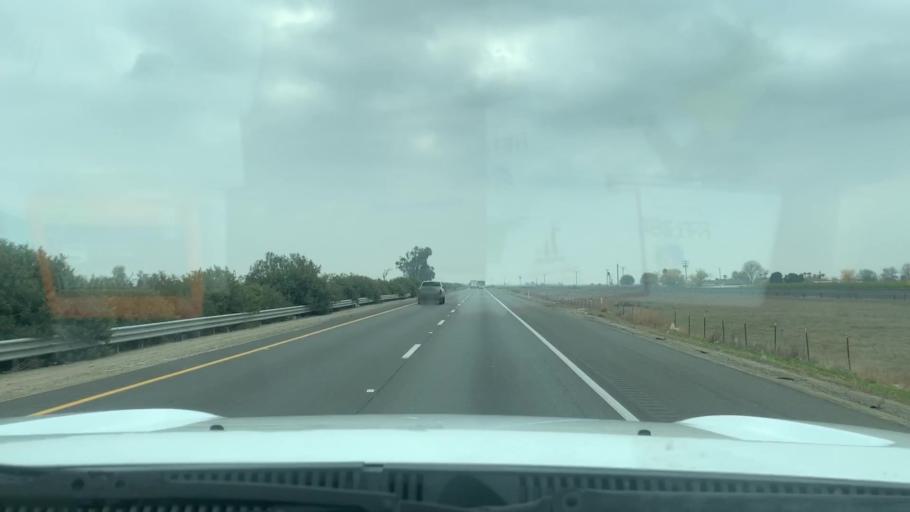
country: US
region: California
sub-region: Tulare County
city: Tipton
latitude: 36.0986
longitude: -119.3227
